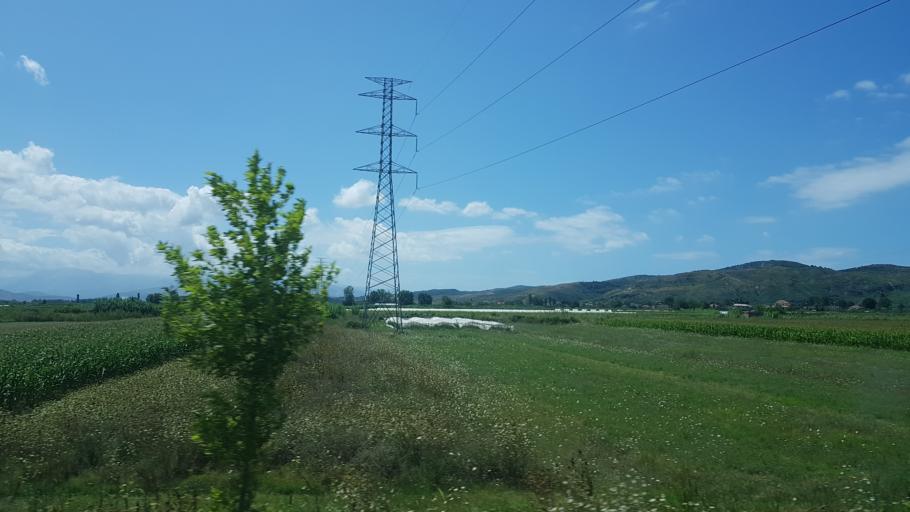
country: AL
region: Fier
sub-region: Rrethi i Fierit
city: Frakulla e Madhe
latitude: 40.6052
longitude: 19.5473
